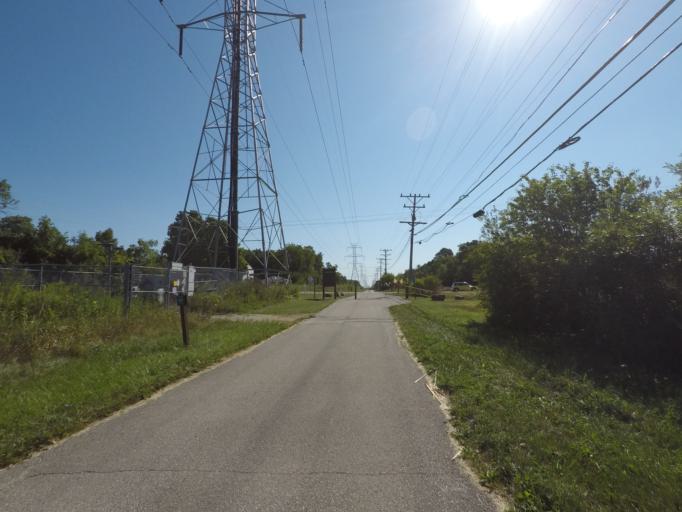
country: US
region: Wisconsin
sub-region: Waukesha County
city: Elm Grove
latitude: 43.0101
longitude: -88.0871
